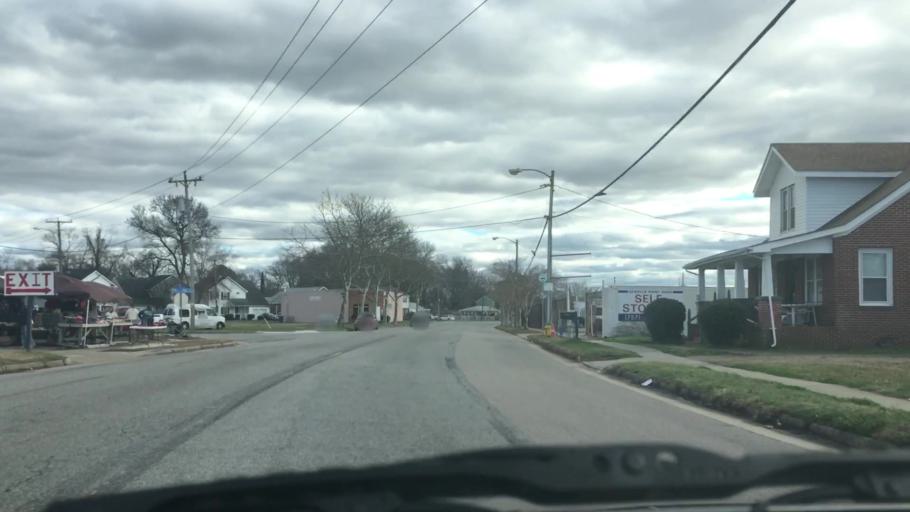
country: US
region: Virginia
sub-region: City of Norfolk
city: Norfolk
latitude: 36.9132
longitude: -76.2478
